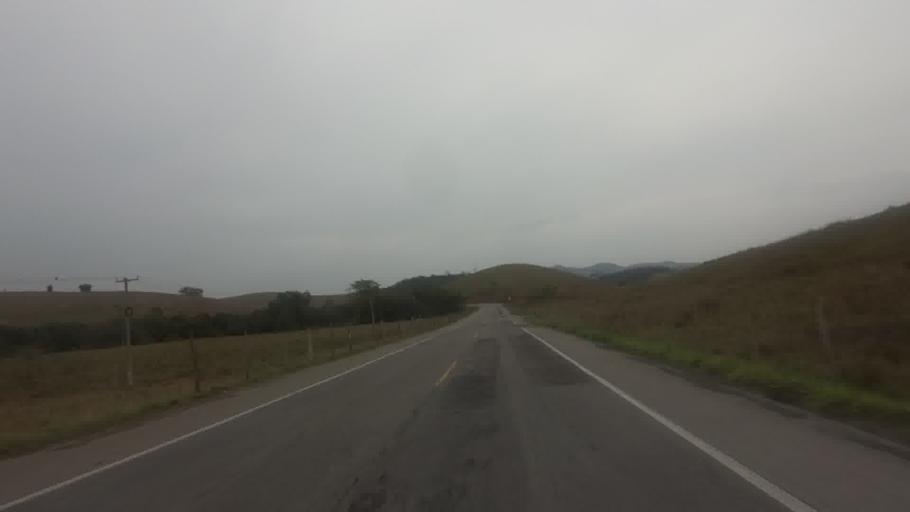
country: BR
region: Rio de Janeiro
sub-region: Santo Antonio De Padua
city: Santo Antonio de Padua
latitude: -21.6569
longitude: -42.3140
